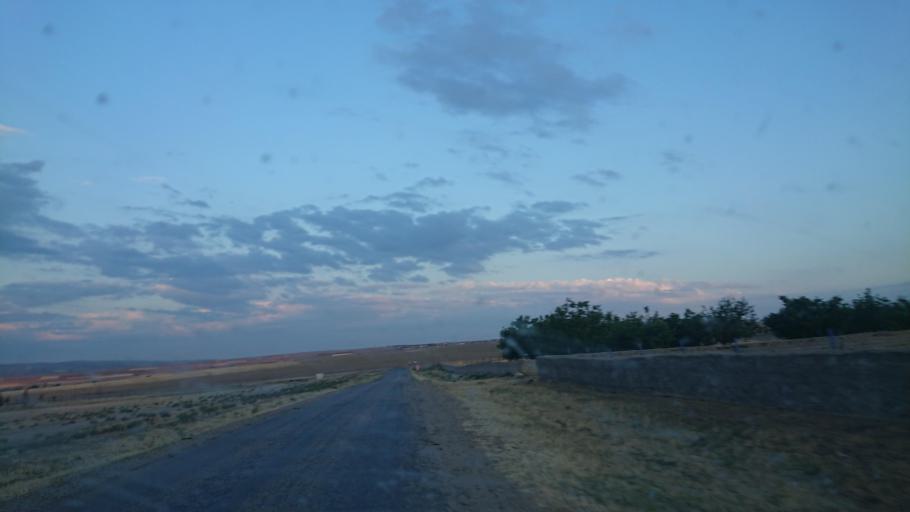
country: TR
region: Aksaray
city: Balci
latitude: 38.8249
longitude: 34.0993
